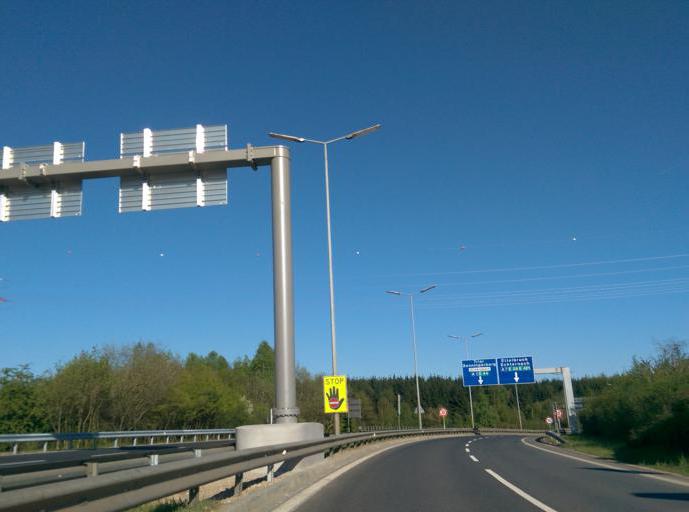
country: LU
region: Luxembourg
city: Kirchberg
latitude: 49.6365
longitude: 6.1810
